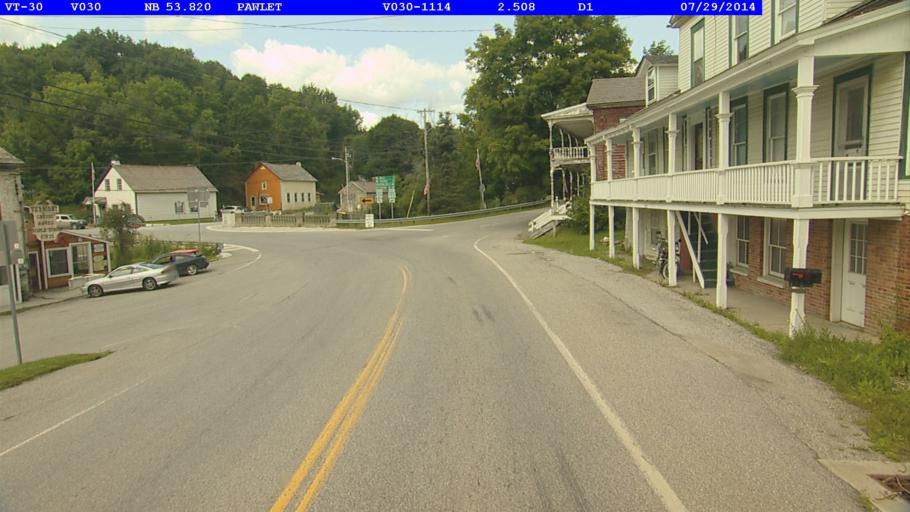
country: US
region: New York
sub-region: Washington County
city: Granville
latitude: 43.3462
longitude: -73.1772
